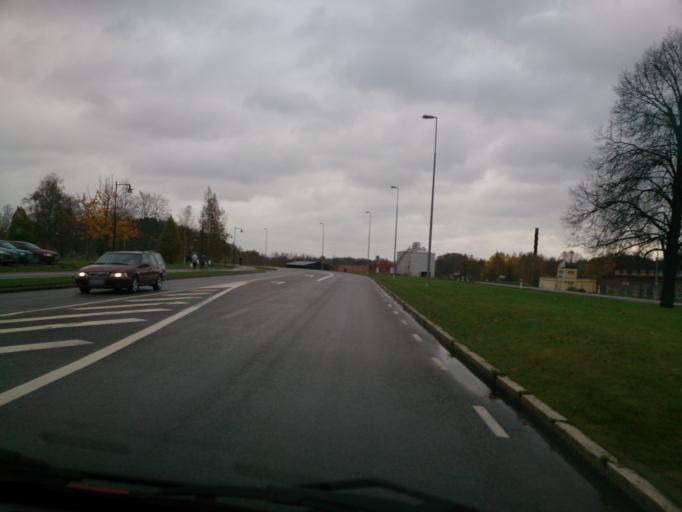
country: SE
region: OEstergoetland
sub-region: Atvidabergs Kommun
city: Atvidaberg
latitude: 58.2027
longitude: 16.0029
